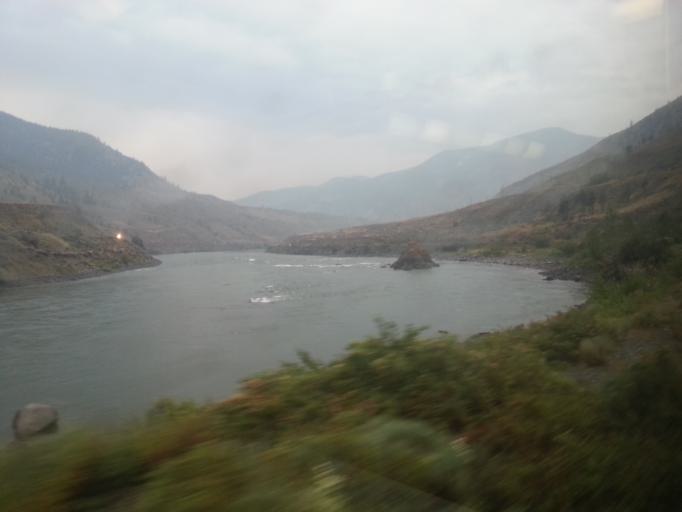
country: CA
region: British Columbia
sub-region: Thompson-Nicola Regional District
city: Ashcroft
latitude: 50.4498
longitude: -121.3093
